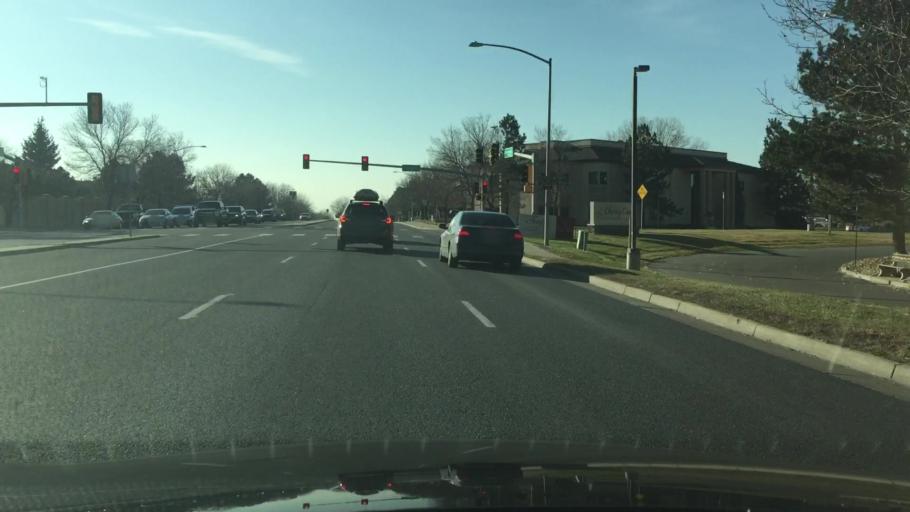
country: US
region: Colorado
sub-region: Arapahoe County
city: Dove Valley
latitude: 39.6532
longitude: -104.8193
